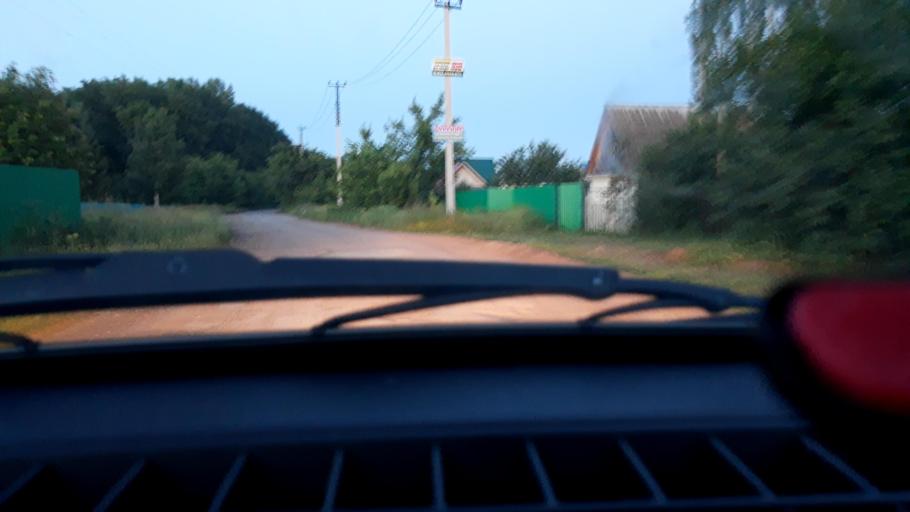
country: RU
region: Bashkortostan
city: Avdon
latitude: 54.4659
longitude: 55.8288
